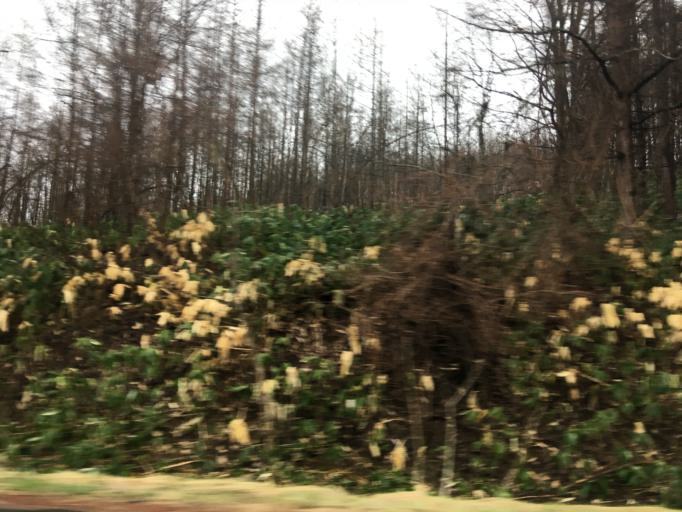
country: JP
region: Hokkaido
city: Nayoro
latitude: 44.0736
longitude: 142.4153
